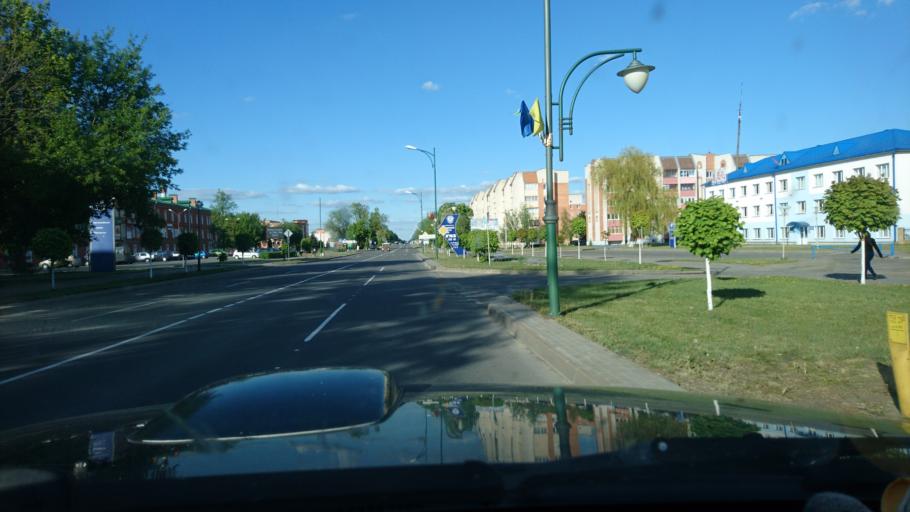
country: BY
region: Brest
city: Byaroza
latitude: 52.5261
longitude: 24.9683
